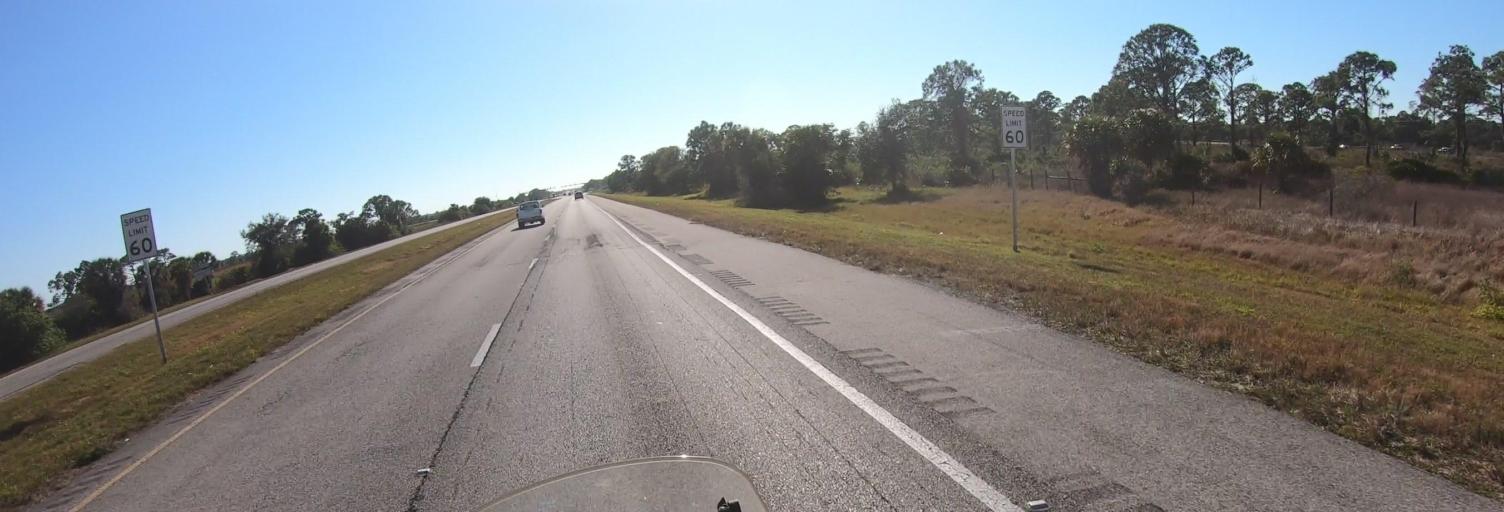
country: US
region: Florida
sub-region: Sarasota County
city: Laurel
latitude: 27.1870
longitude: -82.4421
